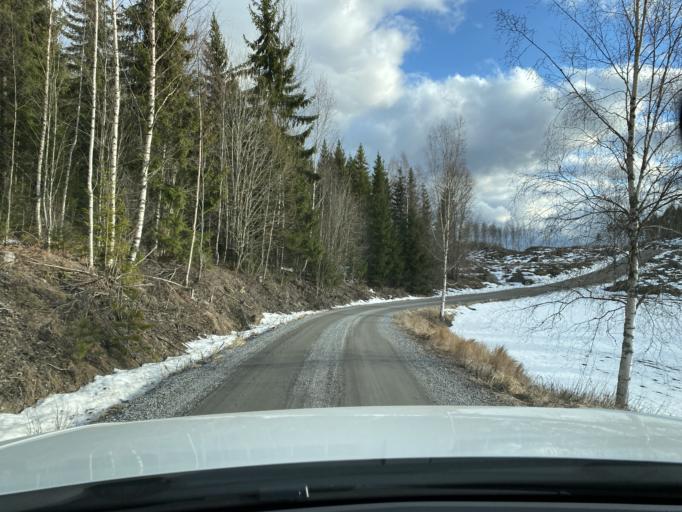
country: FI
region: Pirkanmaa
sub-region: Lounais-Pirkanmaa
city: Mouhijaervi
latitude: 61.4378
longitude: 22.9662
